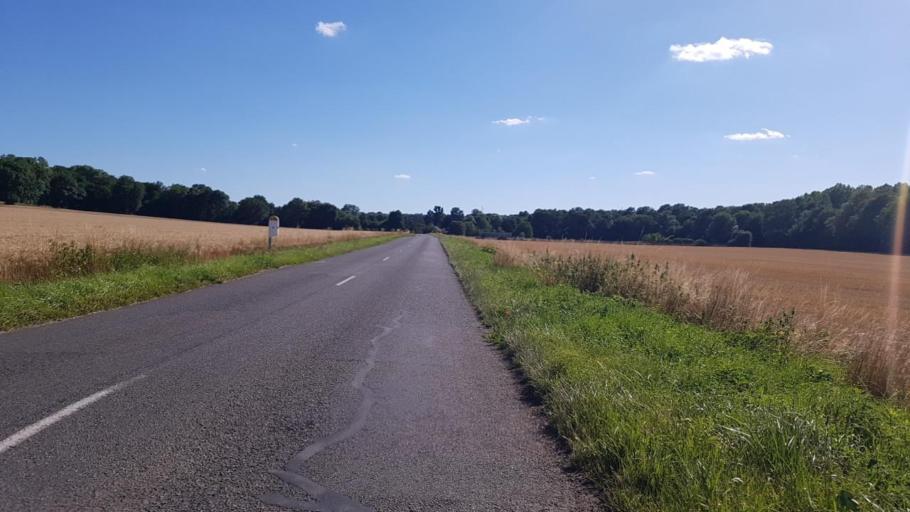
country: FR
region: Ile-de-France
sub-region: Departement de Seine-et-Marne
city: Coupvray
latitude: 48.9142
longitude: 2.7864
